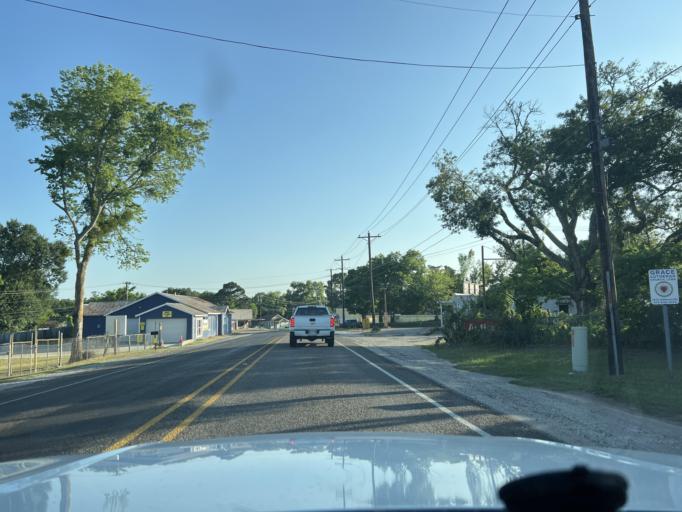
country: US
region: Texas
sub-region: Washington County
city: Brenham
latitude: 30.1739
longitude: -96.3895
